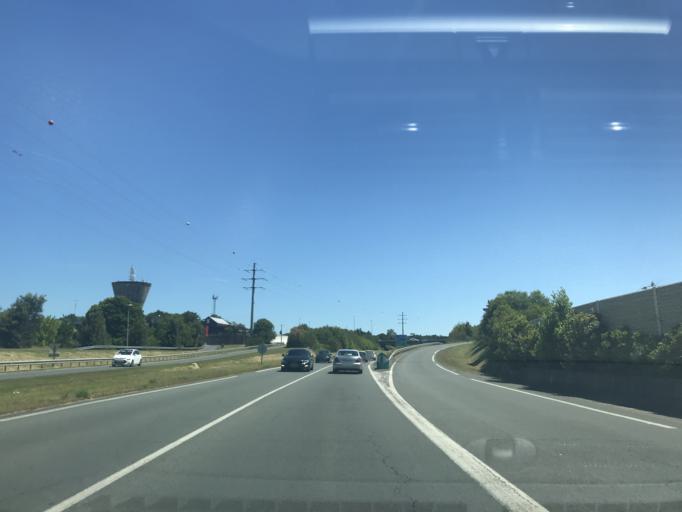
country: FR
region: Poitou-Charentes
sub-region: Departement de la Charente-Maritime
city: Saint-Georges-de-Didonne
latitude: 45.6281
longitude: -1.0018
